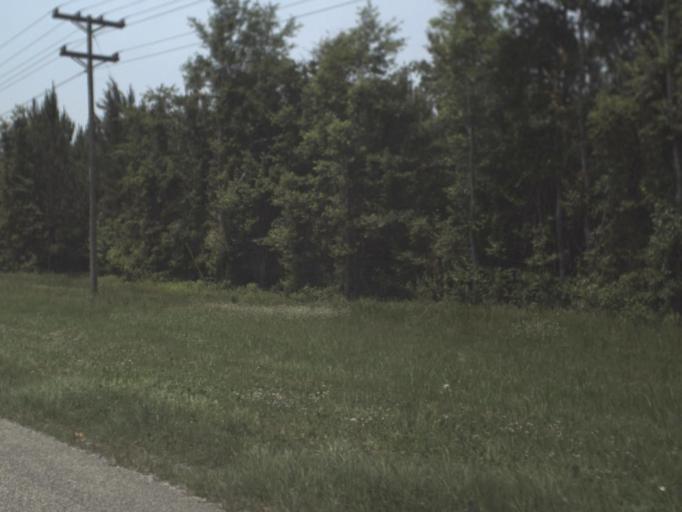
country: US
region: Florida
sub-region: Duval County
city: Baldwin
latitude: 30.1785
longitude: -82.0236
